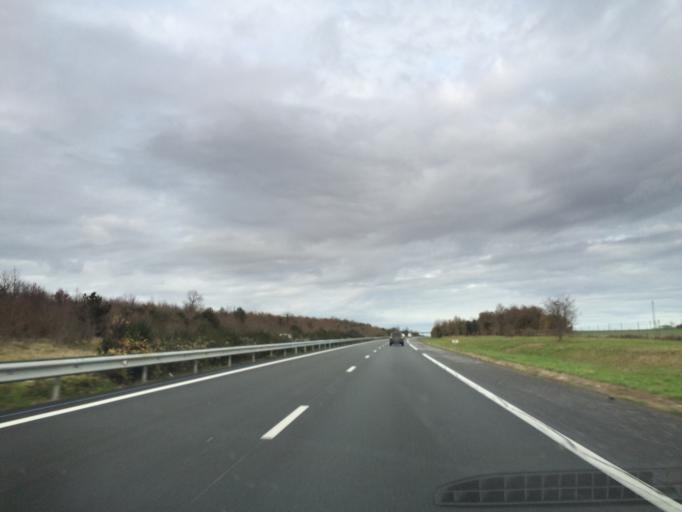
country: FR
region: Poitou-Charentes
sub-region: Departement des Deux-Sevres
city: Beauvoir-sur-Niort
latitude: 46.1763
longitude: -0.5049
